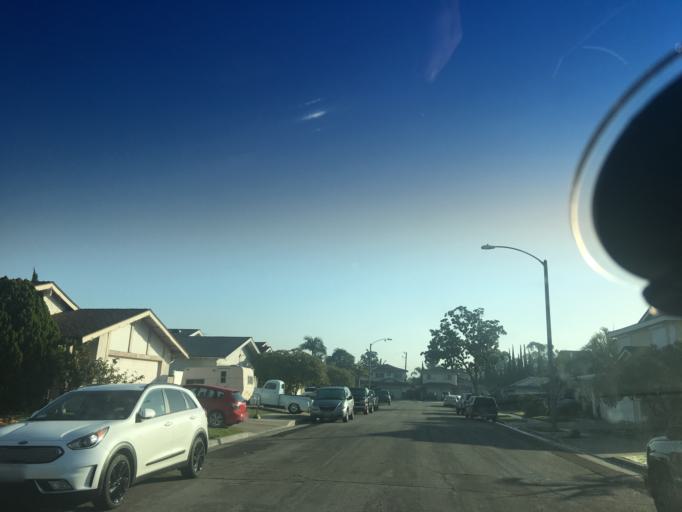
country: US
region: California
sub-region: Orange County
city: Anaheim
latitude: 33.8196
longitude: -117.8797
